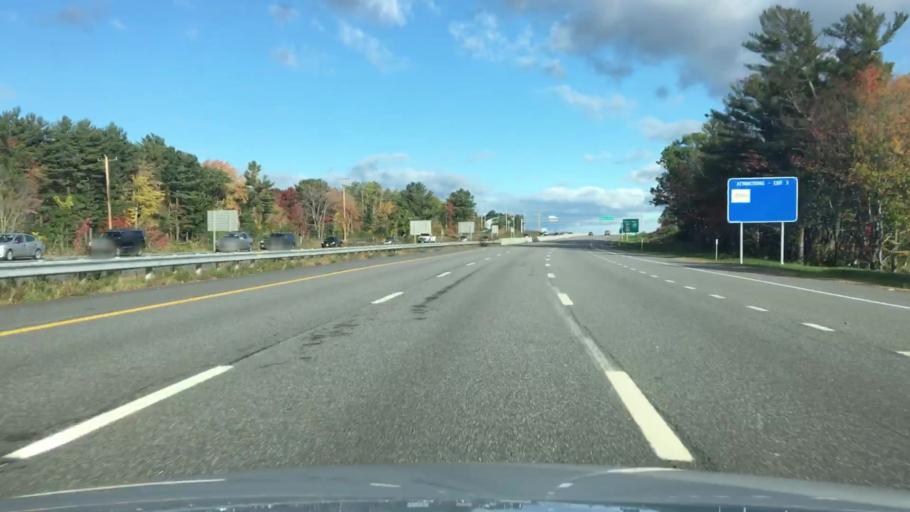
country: US
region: Maine
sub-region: York County
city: South Eliot
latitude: 43.0954
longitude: -70.8076
